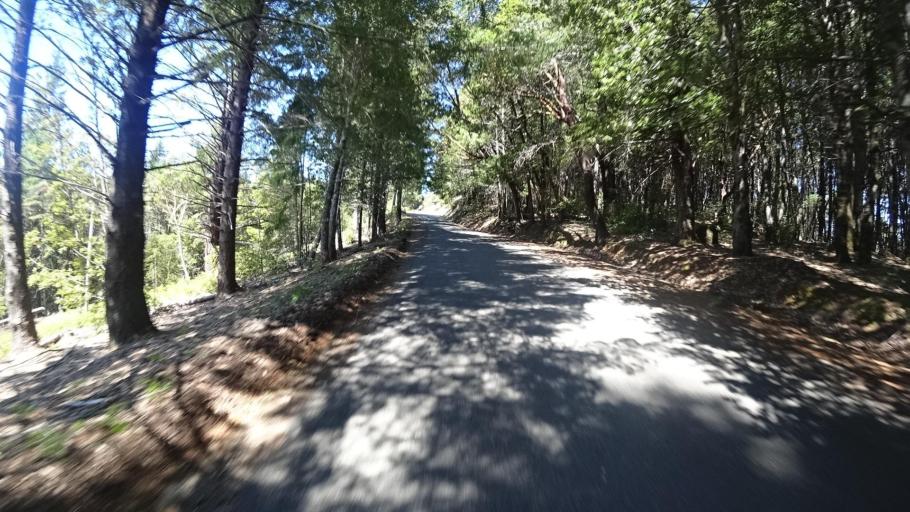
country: US
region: California
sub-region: Humboldt County
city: Redway
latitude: 40.1507
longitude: -124.0261
